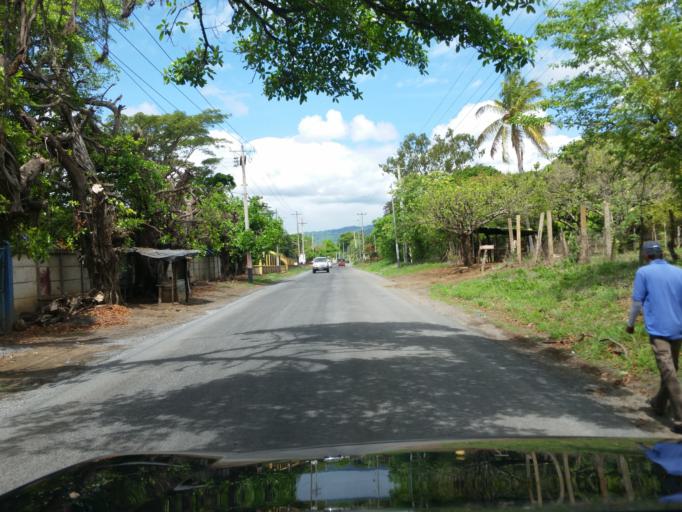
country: NI
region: Masaya
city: Ticuantepe
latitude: 12.0722
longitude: -86.1812
